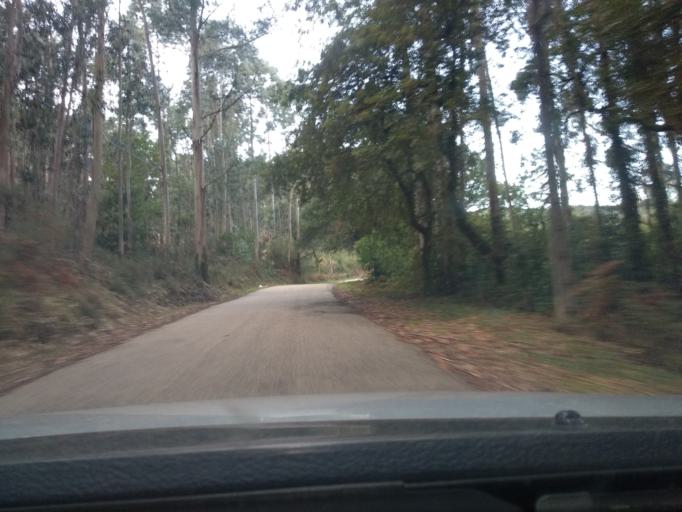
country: ES
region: Galicia
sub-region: Provincia de Pontevedra
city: Moana
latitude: 42.2998
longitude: -8.6967
